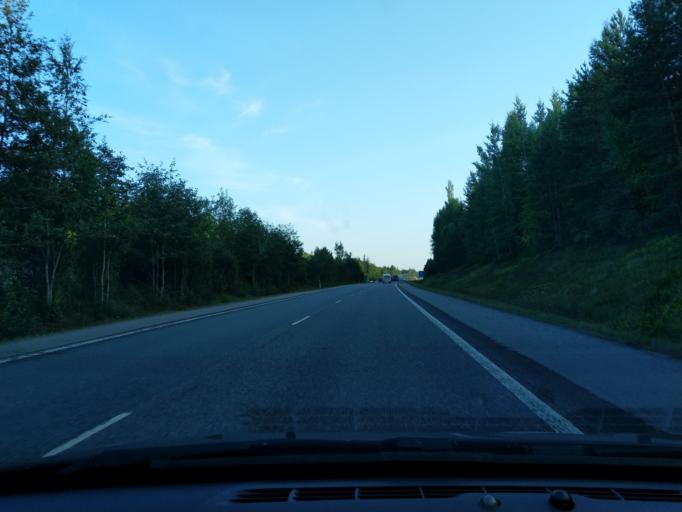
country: FI
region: Uusimaa
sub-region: Porvoo
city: Pukkila
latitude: 60.7859
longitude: 25.4859
